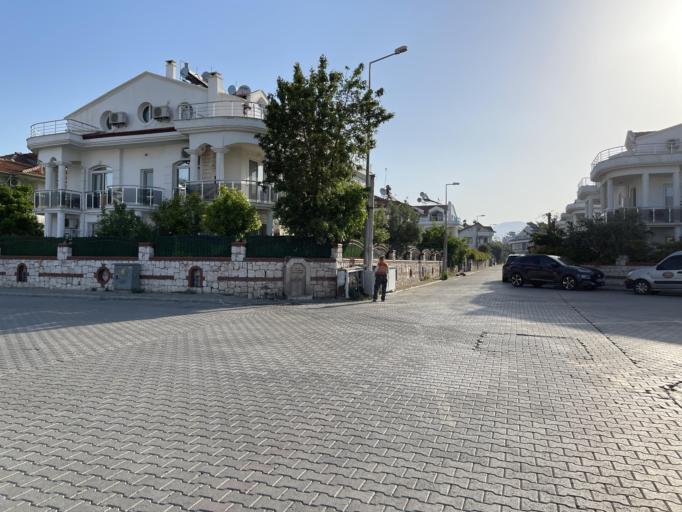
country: TR
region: Mugla
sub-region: Fethiye
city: Fethiye
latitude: 36.6576
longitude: 29.1229
